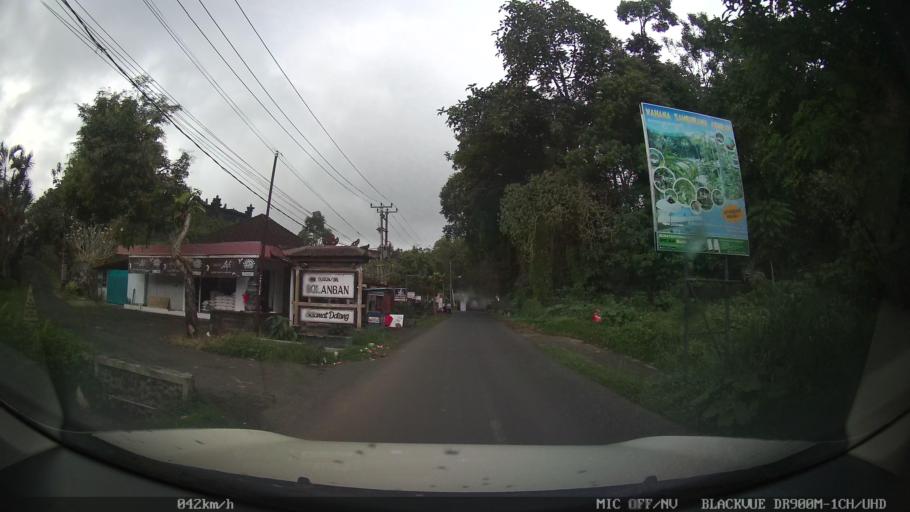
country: ID
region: Bali
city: Empalan
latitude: -8.3800
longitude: 115.1522
